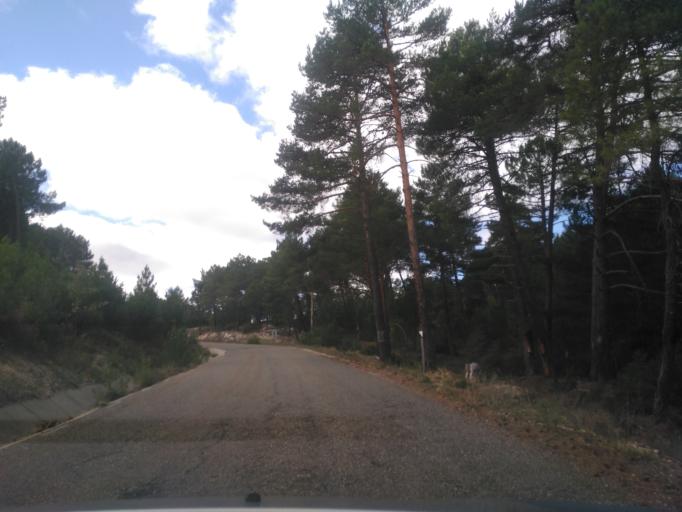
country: ES
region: Castille and Leon
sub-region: Provincia de Soria
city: Espejon
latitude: 41.8452
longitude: -3.2367
